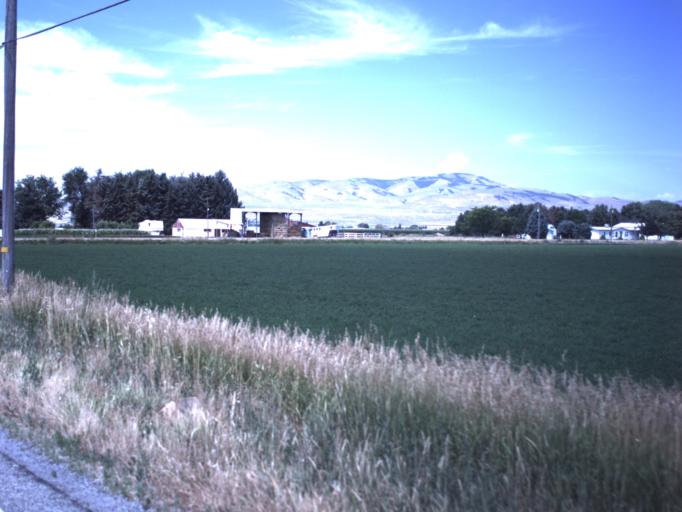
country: US
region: Utah
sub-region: Box Elder County
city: Elwood
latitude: 41.7125
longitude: -112.1308
